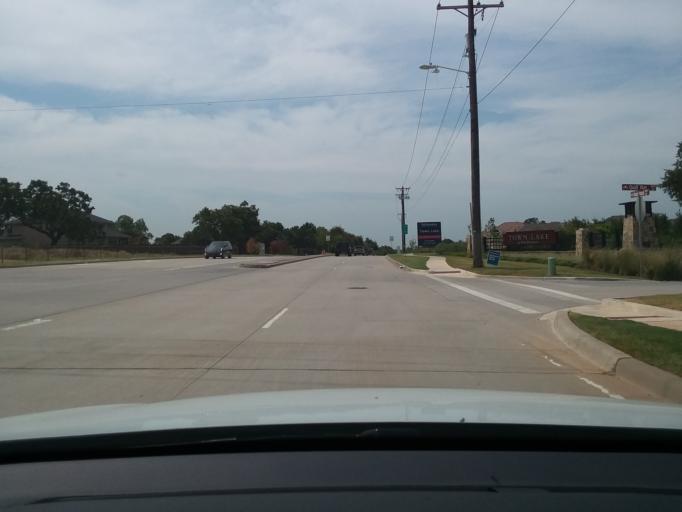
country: US
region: Texas
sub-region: Denton County
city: Flower Mound
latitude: 33.0363
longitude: -97.1053
